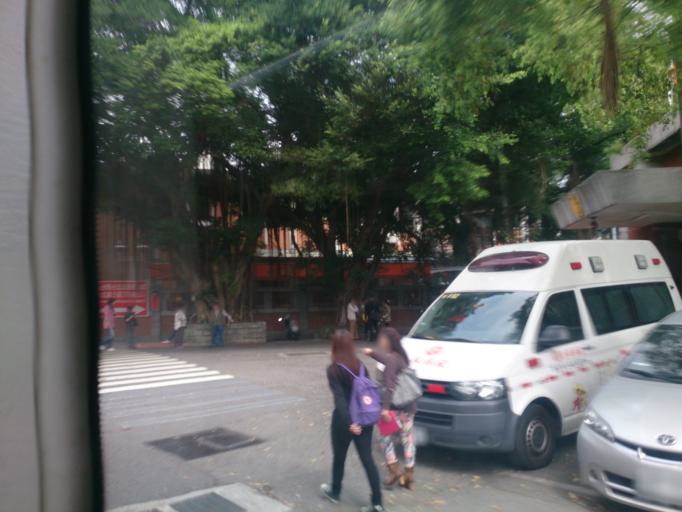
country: TW
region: Taipei
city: Taipei
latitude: 25.0901
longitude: 121.5277
